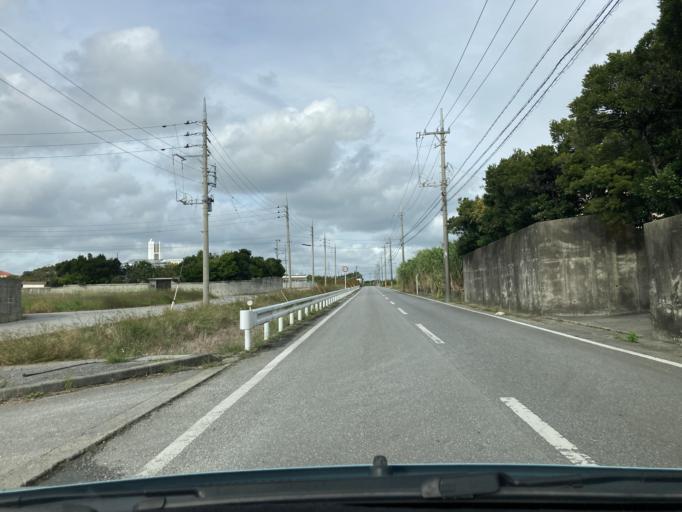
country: JP
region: Okinawa
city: Itoman
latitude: 26.1081
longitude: 127.6882
